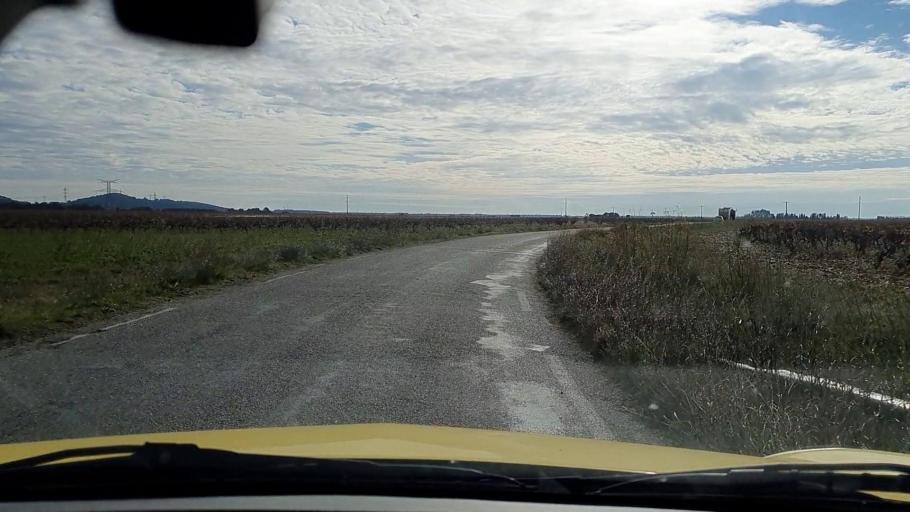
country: FR
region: Languedoc-Roussillon
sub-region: Departement du Gard
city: Jonquieres-Saint-Vincent
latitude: 43.8528
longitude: 4.5758
